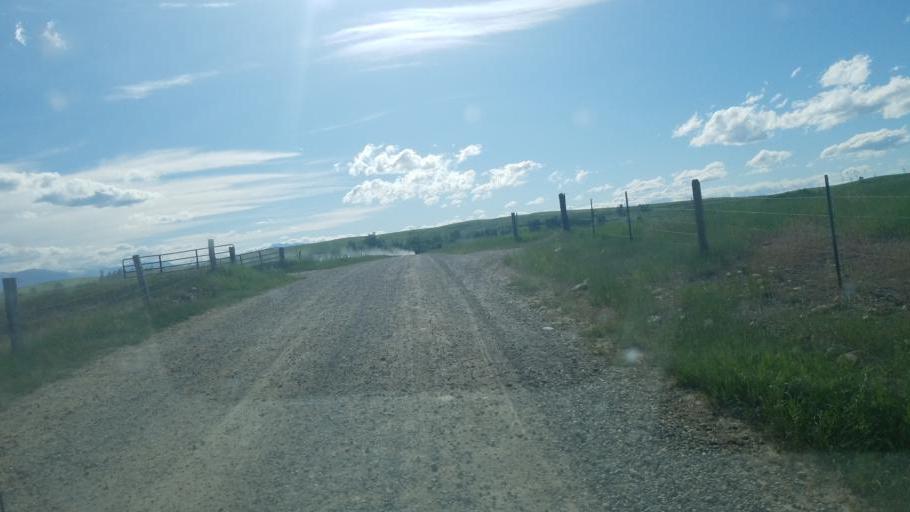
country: US
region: Montana
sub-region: Carbon County
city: Red Lodge
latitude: 45.3636
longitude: -109.1713
